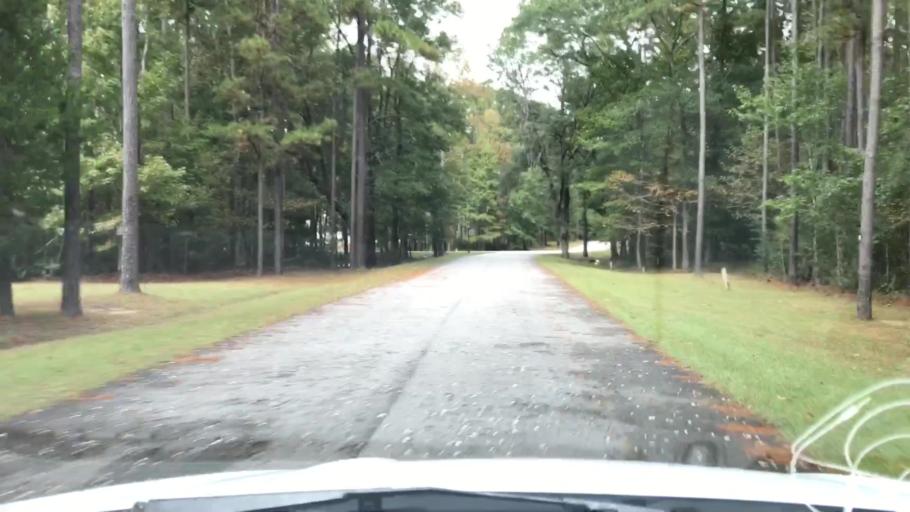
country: US
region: South Carolina
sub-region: Beaufort County
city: Bluffton
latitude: 32.2366
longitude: -80.9273
